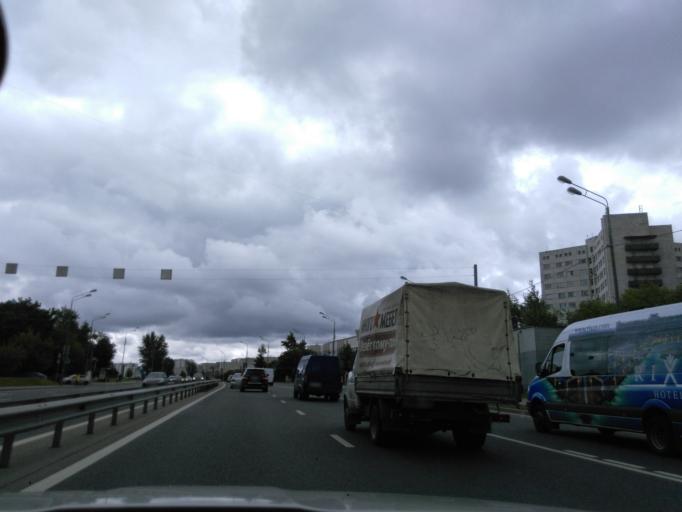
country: RU
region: Moscow
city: Nikol'skoye
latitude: 55.6754
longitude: 37.4850
